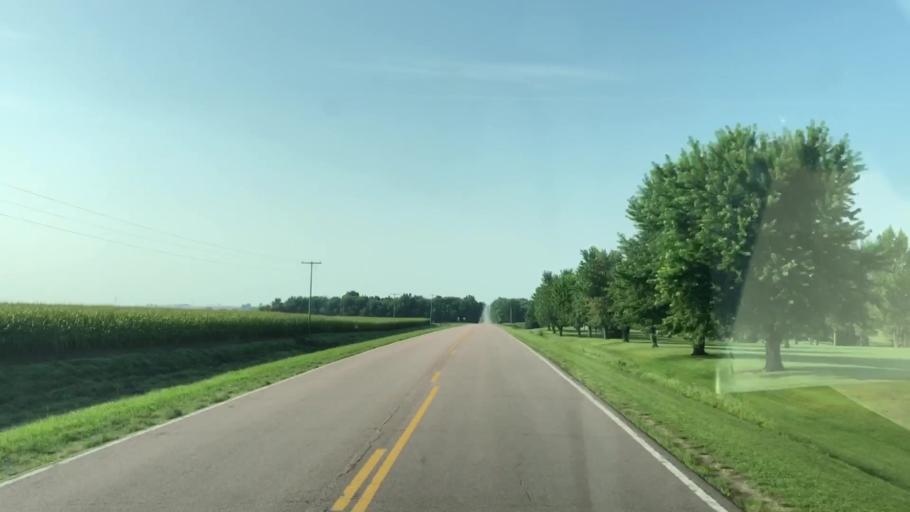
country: US
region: Iowa
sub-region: Lyon County
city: George
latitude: 43.2614
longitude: -96.0001
